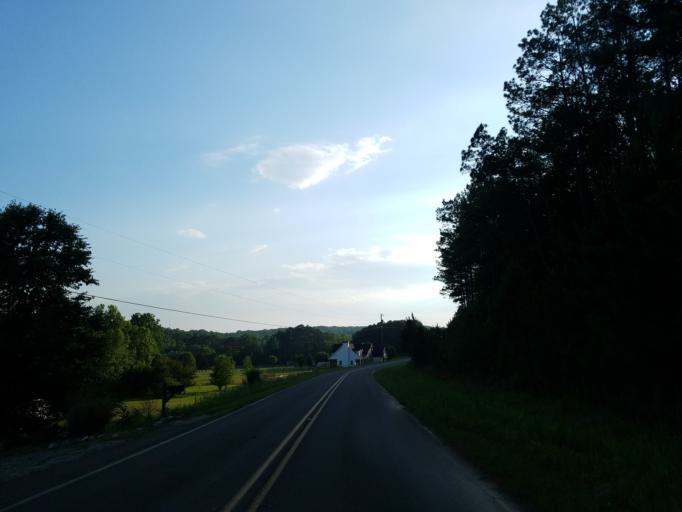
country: US
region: Georgia
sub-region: Cherokee County
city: Ball Ground
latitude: 34.2996
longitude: -84.3715
